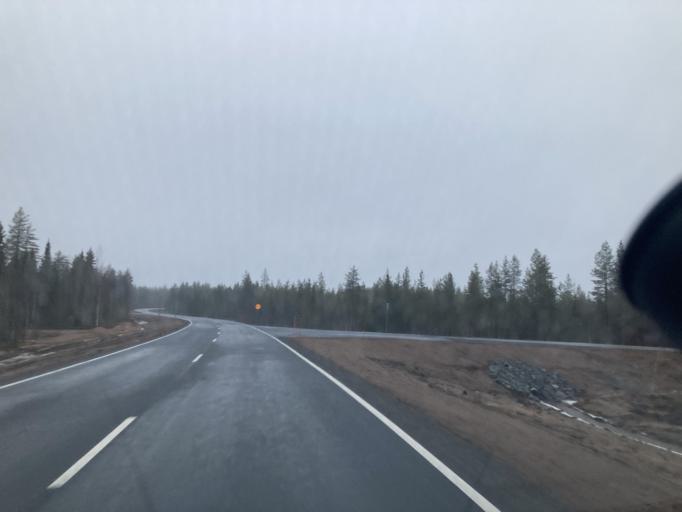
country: FI
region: Lapland
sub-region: Rovaniemi
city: Rovaniemi
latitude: 66.5900
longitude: 25.7986
